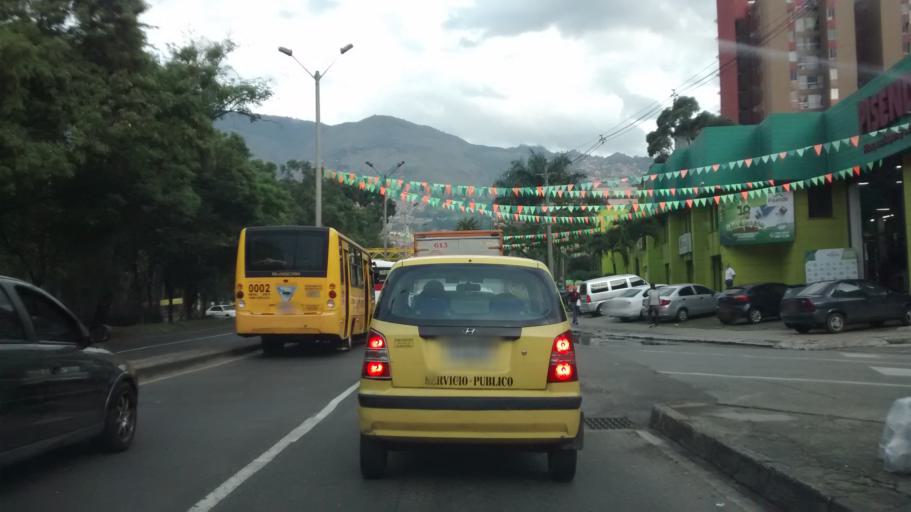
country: CO
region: Antioquia
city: Medellin
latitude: 6.2649
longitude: -75.5702
